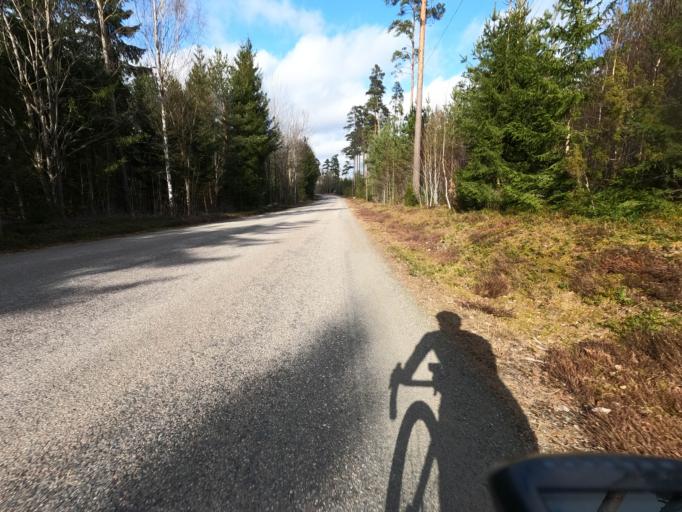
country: SE
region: Kronoberg
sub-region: Alvesta Kommun
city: Vislanda
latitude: 56.7910
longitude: 14.4849
